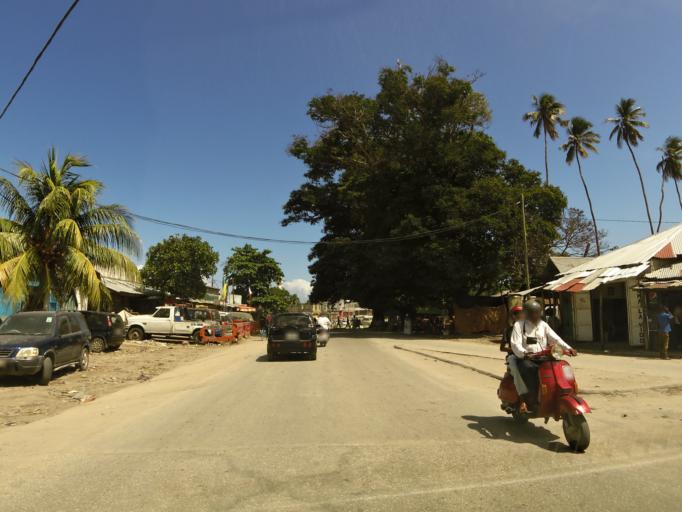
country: TZ
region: Zanzibar Urban/West
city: Zanzibar
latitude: -6.1653
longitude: 39.2047
